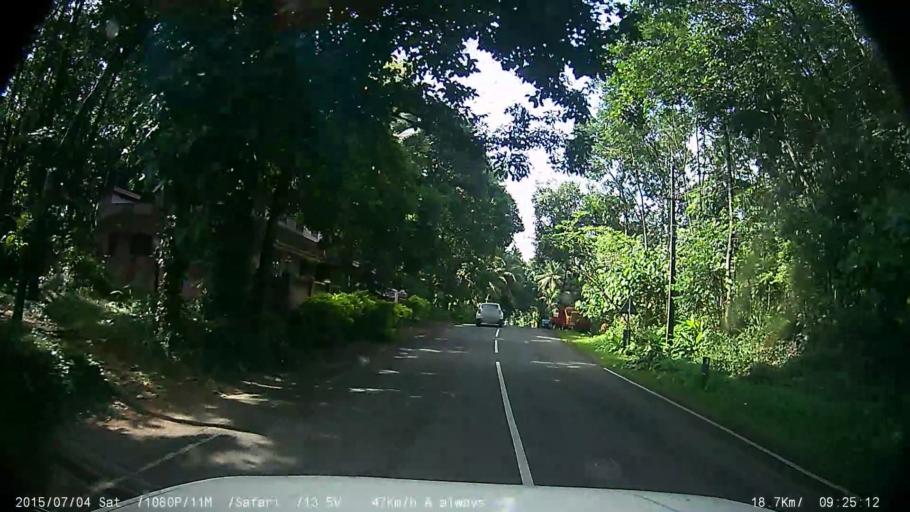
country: IN
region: Kerala
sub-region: Kottayam
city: Palackattumala
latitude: 9.6649
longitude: 76.6090
